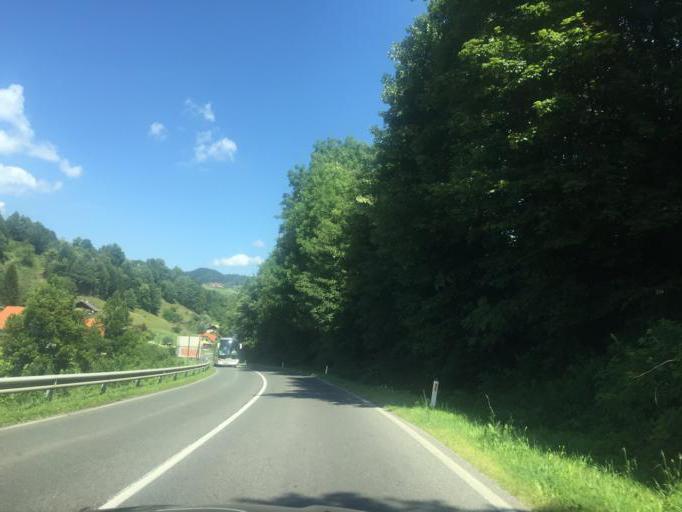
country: SI
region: Zagorje ob Savi
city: Izlake
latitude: 46.1885
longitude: 14.8859
